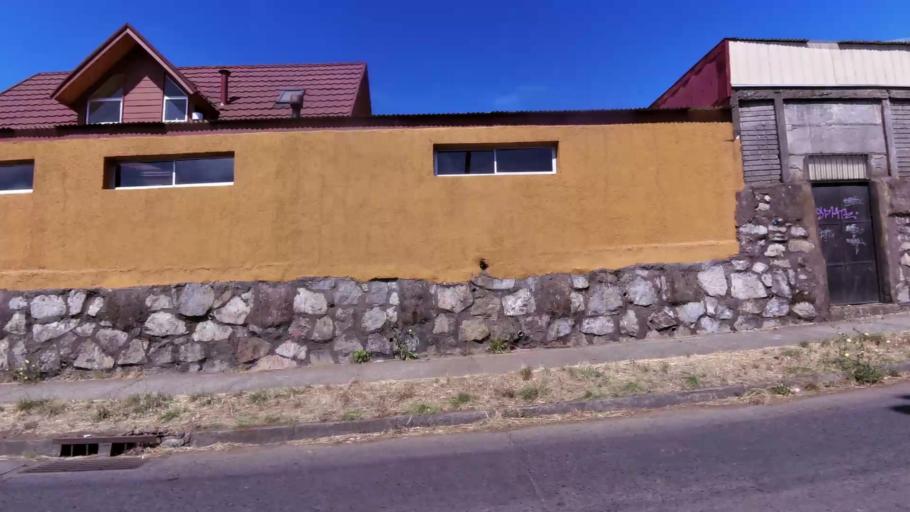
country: CL
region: Biobio
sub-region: Provincia de Concepcion
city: Concepcion
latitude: -36.7813
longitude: -73.0418
